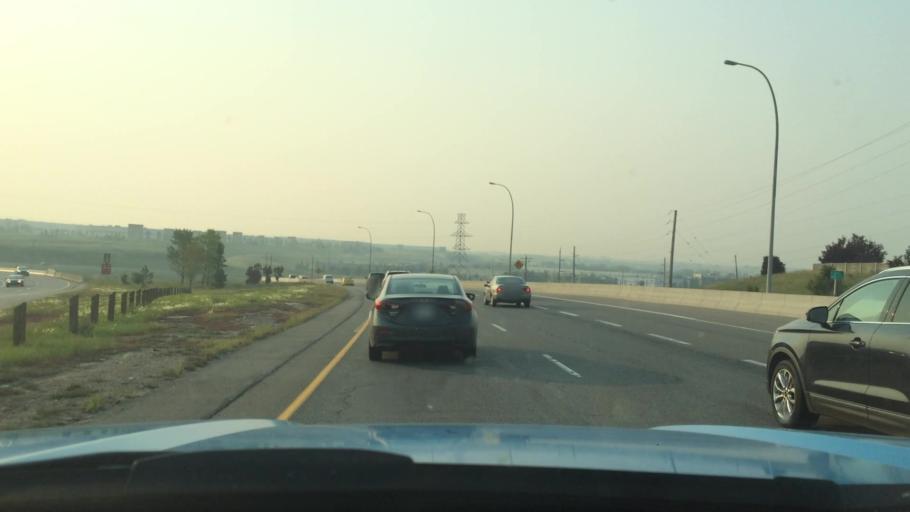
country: CA
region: Alberta
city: Calgary
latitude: 51.1263
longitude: -114.0509
